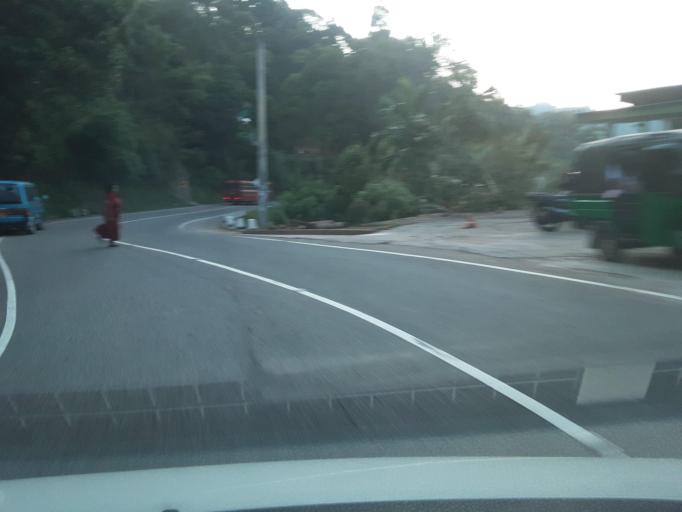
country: LK
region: Uva
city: Badulla
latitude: 6.9205
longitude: 80.9629
